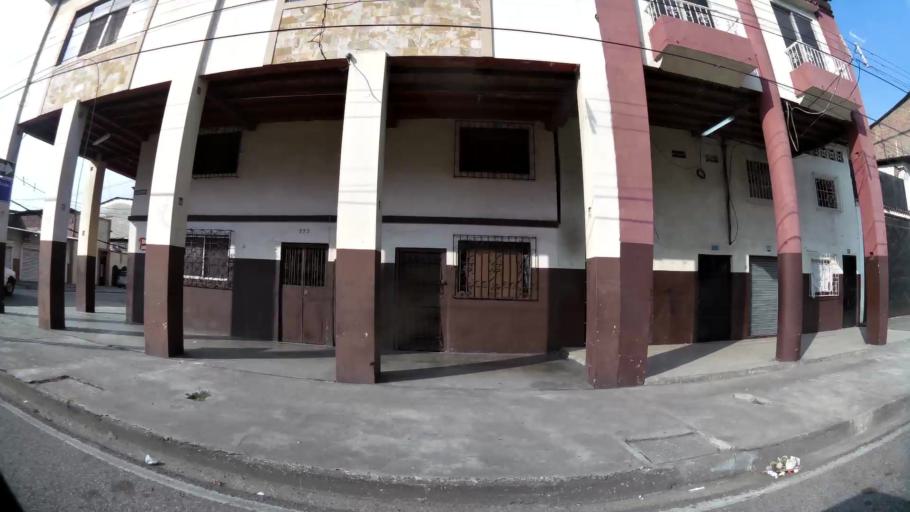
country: EC
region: Guayas
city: Eloy Alfaro
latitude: -2.1839
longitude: -79.8846
